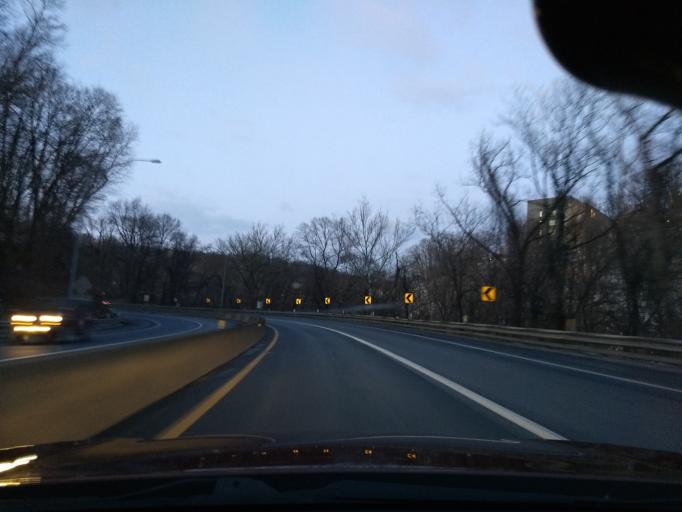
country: US
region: Pennsylvania
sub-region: Northampton County
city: Easton
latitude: 40.6977
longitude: -75.2144
